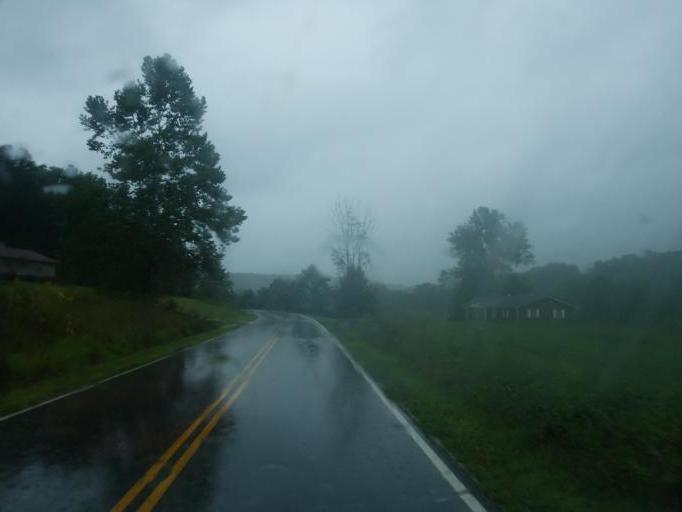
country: US
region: Kentucky
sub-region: Carter County
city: Grayson
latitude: 38.4764
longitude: -83.0330
